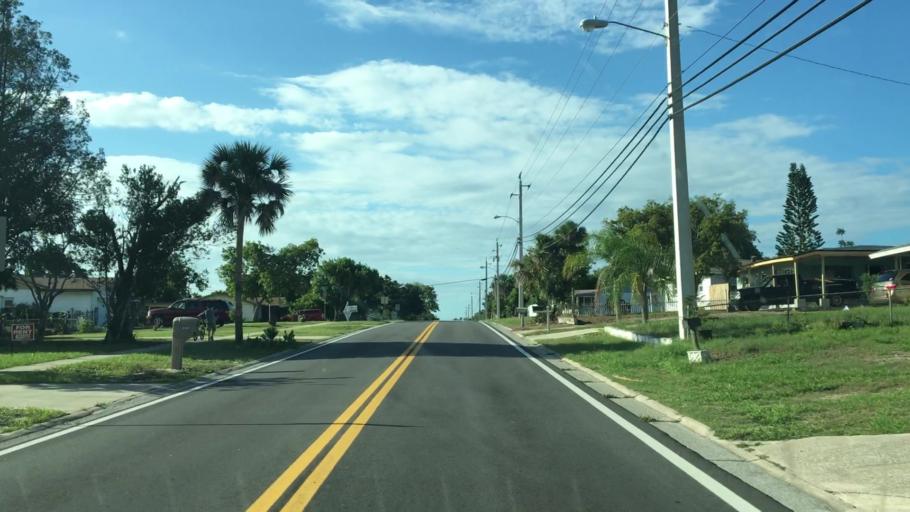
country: US
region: Florida
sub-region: Brevard County
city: Mims
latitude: 28.6287
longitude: -80.8604
